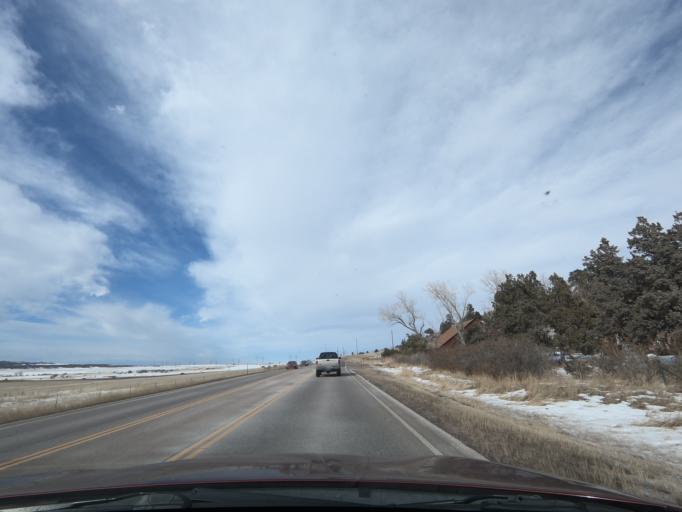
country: US
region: Colorado
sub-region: Elbert County
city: Elizabeth
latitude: 39.2585
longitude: -104.7024
